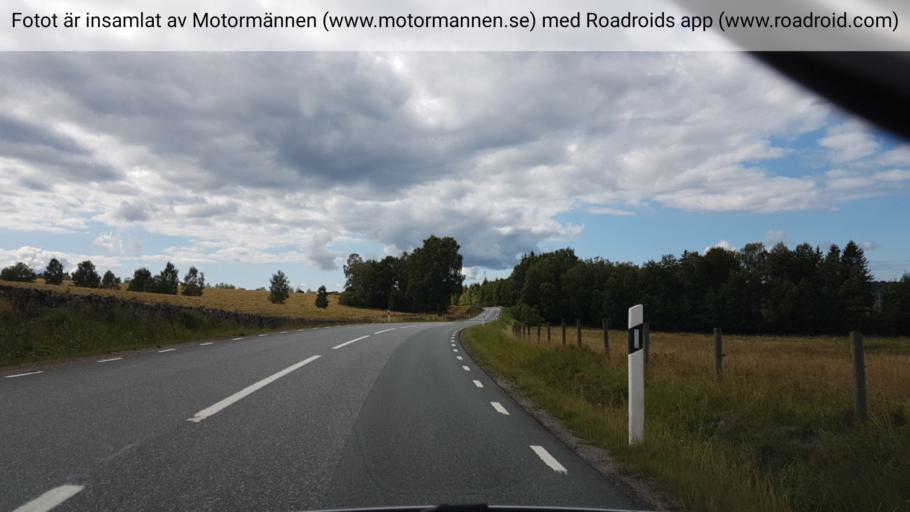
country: SE
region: Joenkoeping
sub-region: Tranas Kommun
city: Tranas
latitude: 57.9991
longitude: 14.8754
